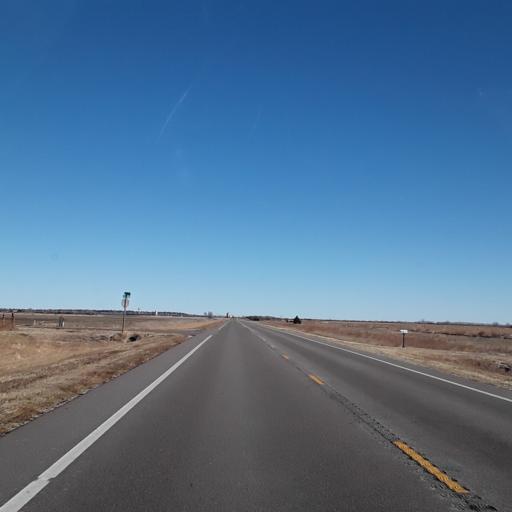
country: US
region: Kansas
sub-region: Pawnee County
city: Larned
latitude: 38.1397
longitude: -99.1510
